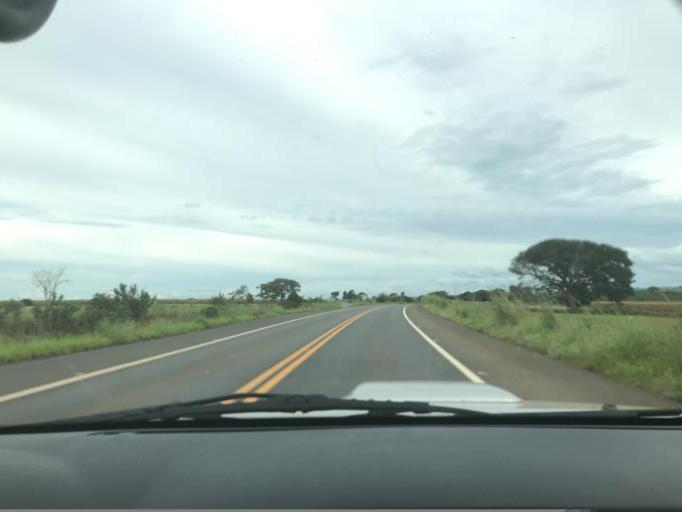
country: BR
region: Minas Gerais
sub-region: Araxa
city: Araxa
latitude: -19.3919
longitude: -46.8559
